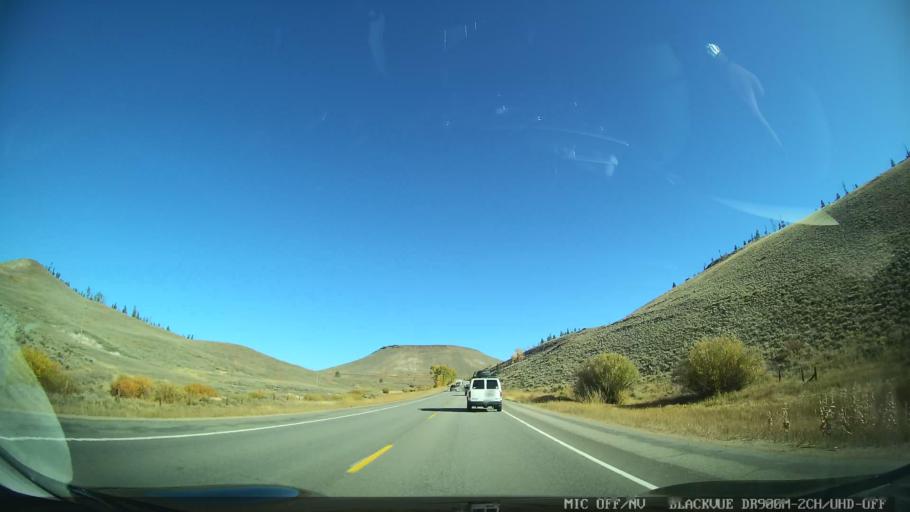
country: US
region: Colorado
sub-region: Grand County
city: Granby
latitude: 40.1275
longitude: -105.8971
